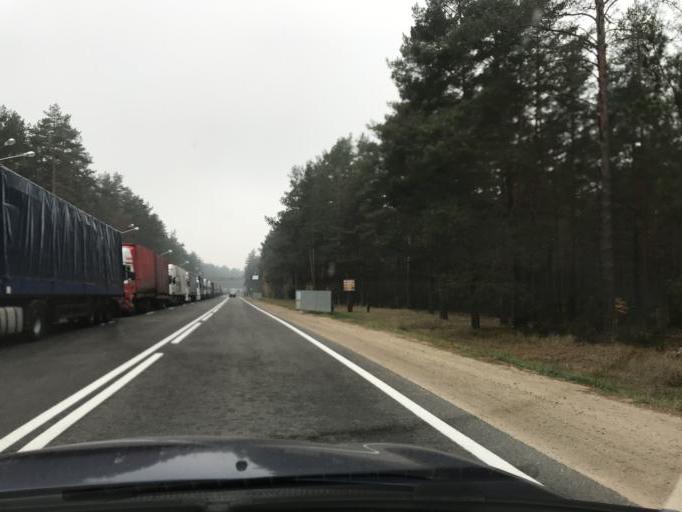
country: LT
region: Alytaus apskritis
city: Druskininkai
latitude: 53.9382
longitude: 23.9561
